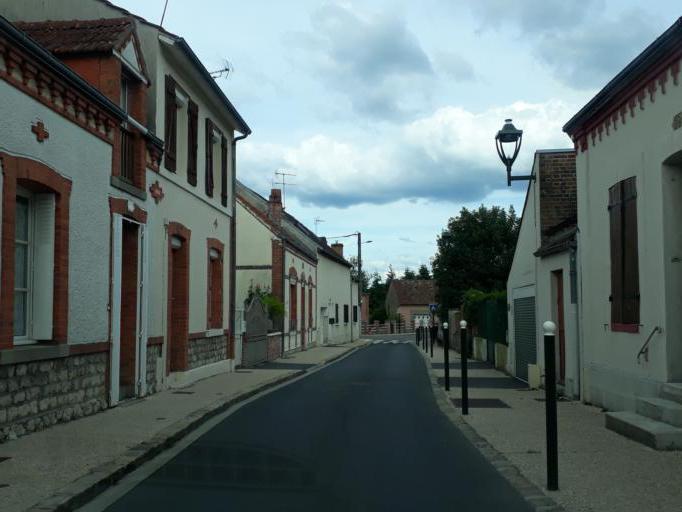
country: FR
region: Centre
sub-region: Departement du Loiret
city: La Ferte-Saint-Aubin
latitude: 47.7230
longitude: 1.9424
